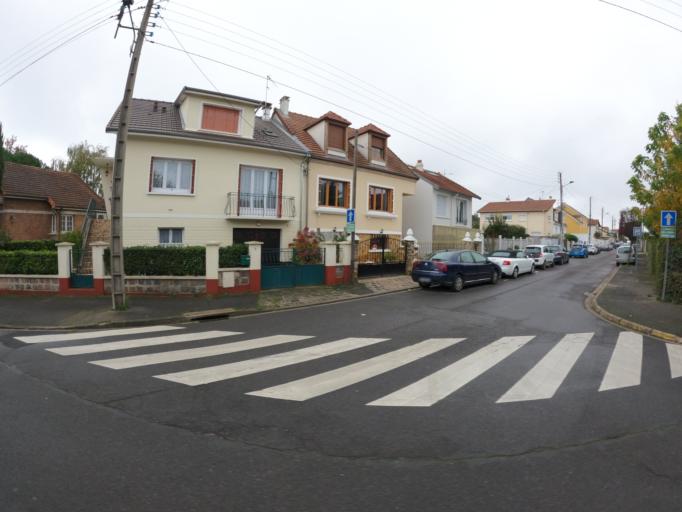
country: FR
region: Ile-de-France
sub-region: Departement du Val-de-Marne
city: Ormesson-sur-Marne
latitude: 48.7888
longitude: 2.5400
